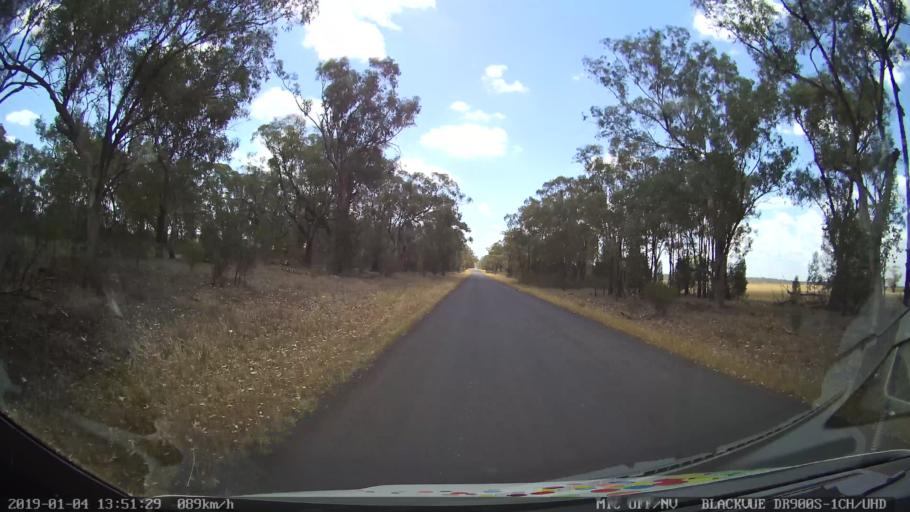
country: AU
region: New South Wales
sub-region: Dubbo Municipality
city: Dubbo
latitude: -32.4063
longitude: 148.5710
